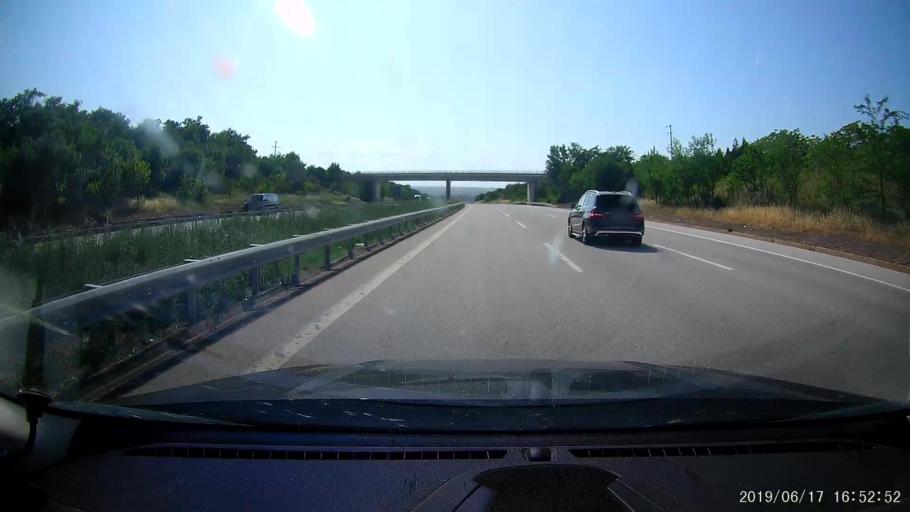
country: TR
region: Kirklareli
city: Inece
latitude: 41.5592
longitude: 27.0402
